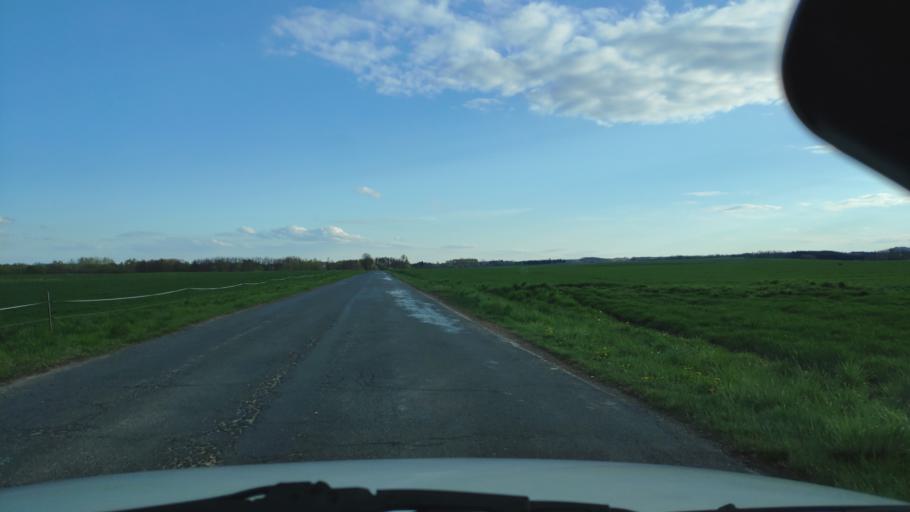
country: HU
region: Zala
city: Zalakomar
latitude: 46.4725
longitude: 17.1275
